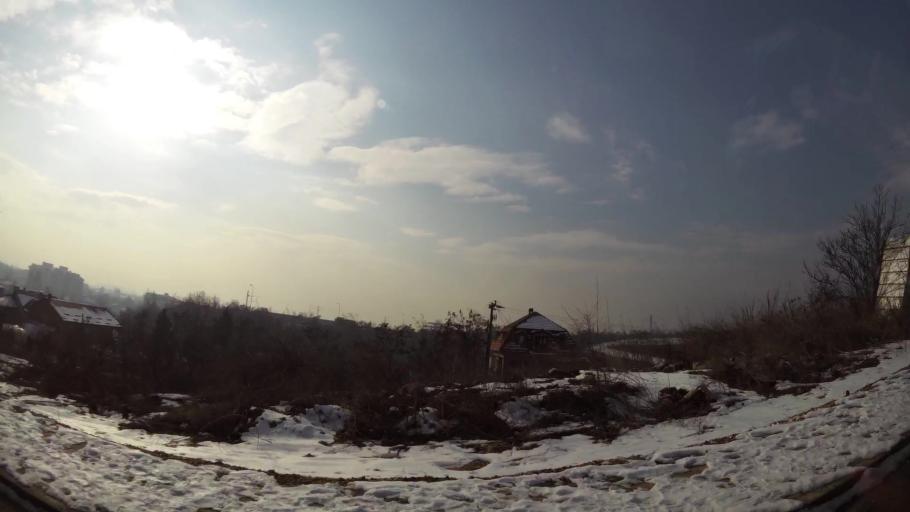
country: MK
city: Creshevo
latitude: 42.0055
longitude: 21.4953
